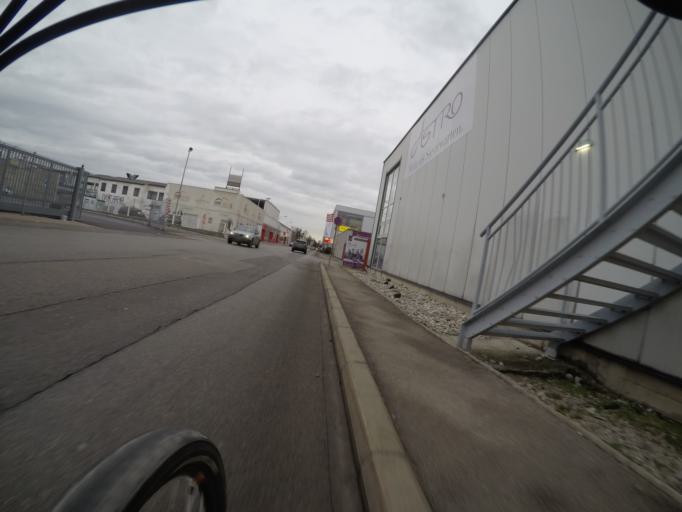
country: AT
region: Lower Austria
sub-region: Politischer Bezirk Modling
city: Vosendorf
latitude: 48.1272
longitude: 16.3229
